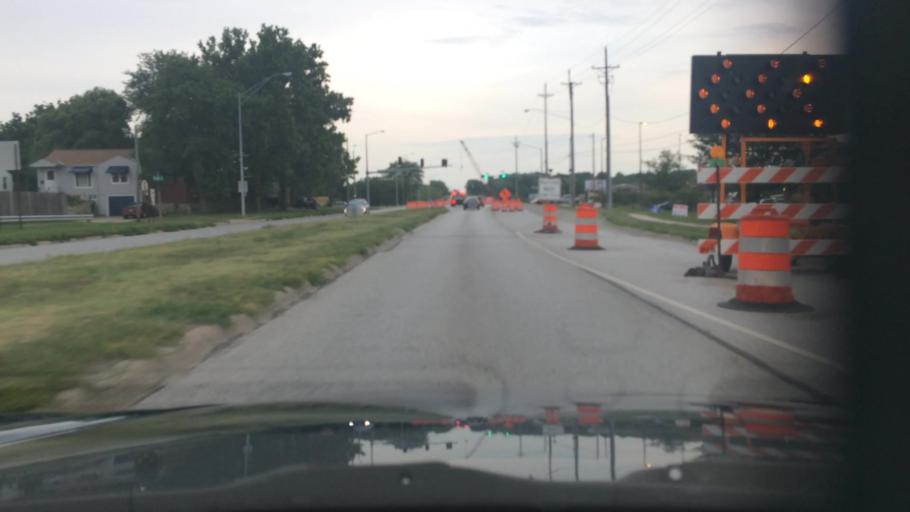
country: US
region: Nebraska
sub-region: Douglas County
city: Ralston
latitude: 41.2021
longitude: -96.0430
